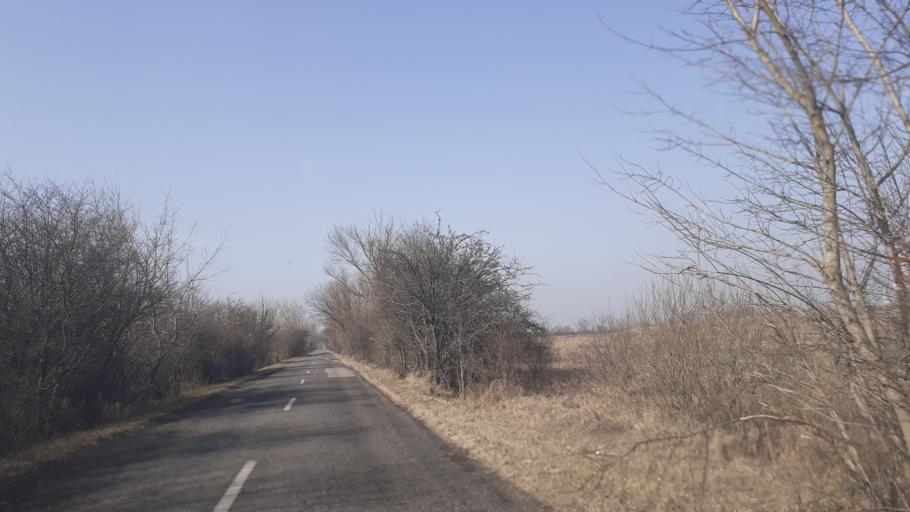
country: HU
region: Pest
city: Dabas
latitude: 47.0500
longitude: 19.3163
